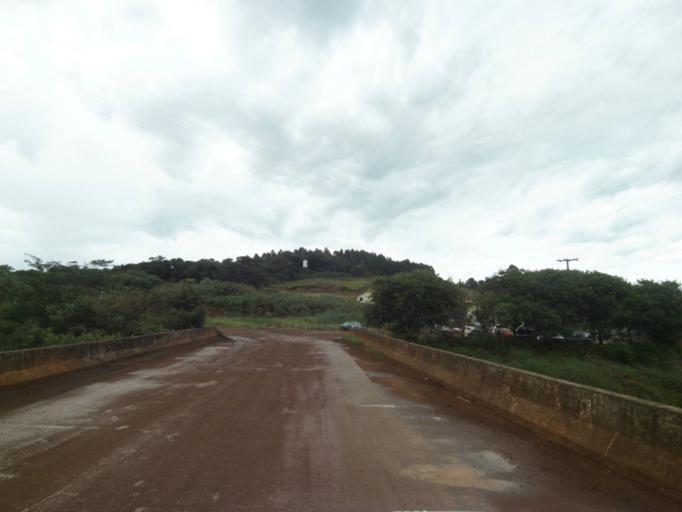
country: BR
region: Parana
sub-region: Guaraniacu
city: Guaraniacu
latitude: -25.1169
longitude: -52.8510
